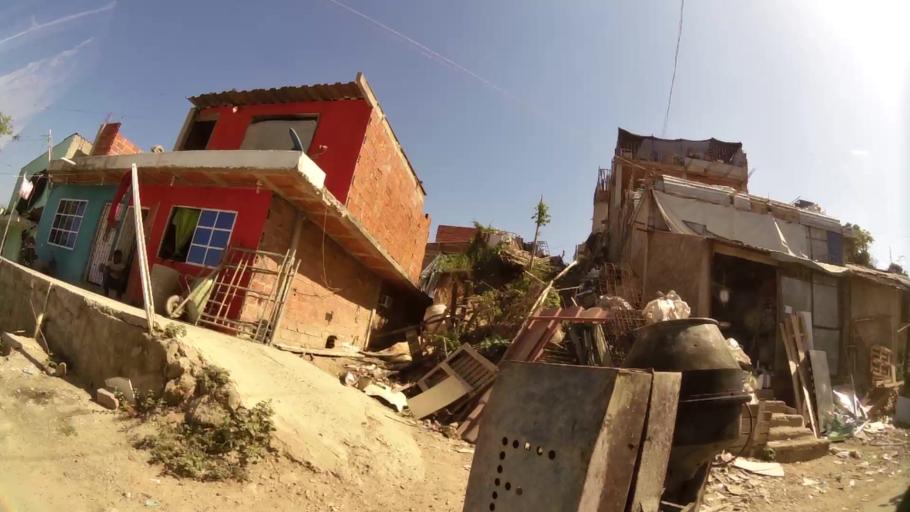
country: CO
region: Bolivar
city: Cartagena
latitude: 10.3714
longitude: -75.4955
